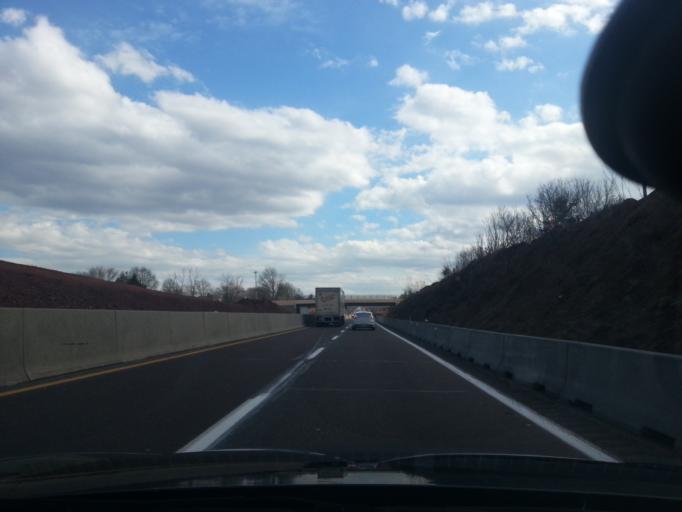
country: US
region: Pennsylvania
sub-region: Montgomery County
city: Kulpsville
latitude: 40.2298
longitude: -75.3354
